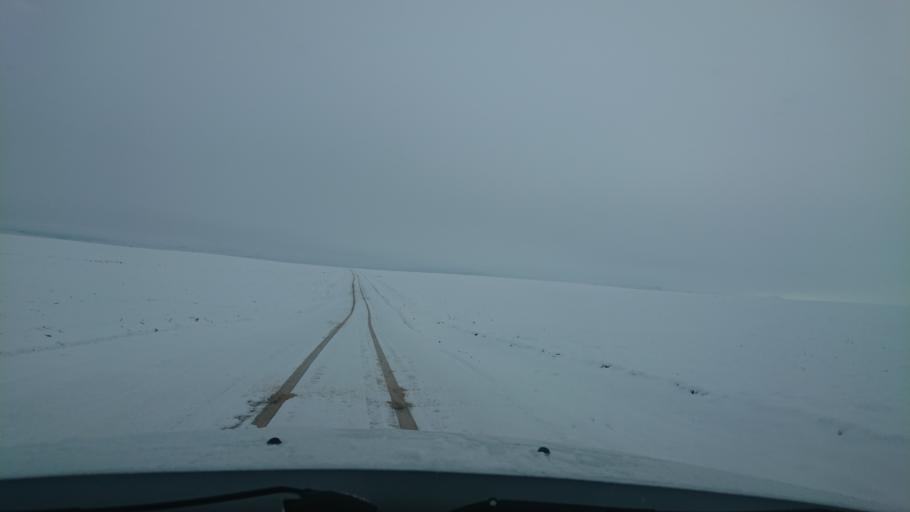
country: TR
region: Aksaray
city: Agacoren
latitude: 38.7412
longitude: 33.8725
